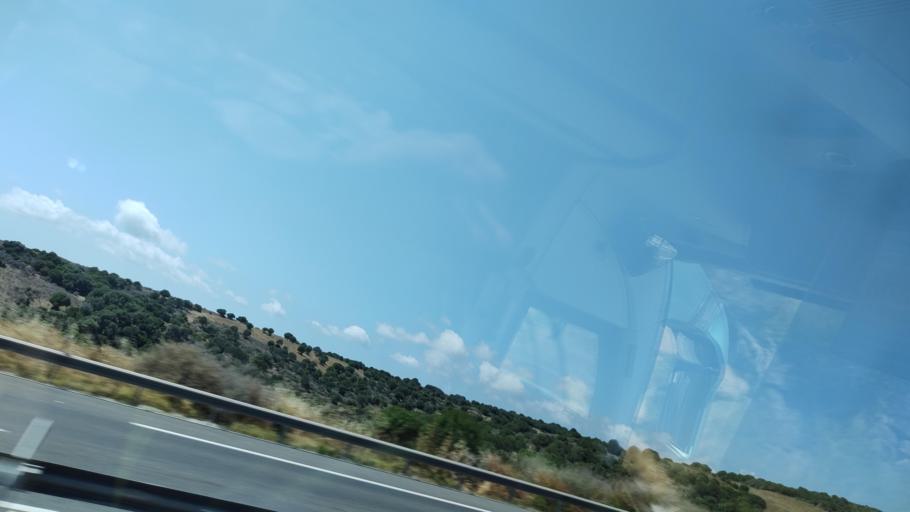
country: ES
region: Andalusia
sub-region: Provincia de Malaga
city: Manilva
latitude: 36.3181
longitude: -5.2720
